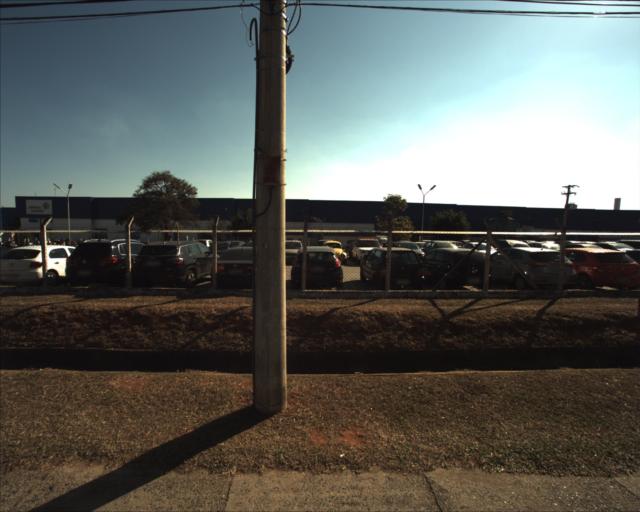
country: BR
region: Sao Paulo
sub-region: Sorocaba
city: Sorocaba
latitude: -23.4391
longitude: -47.4165
